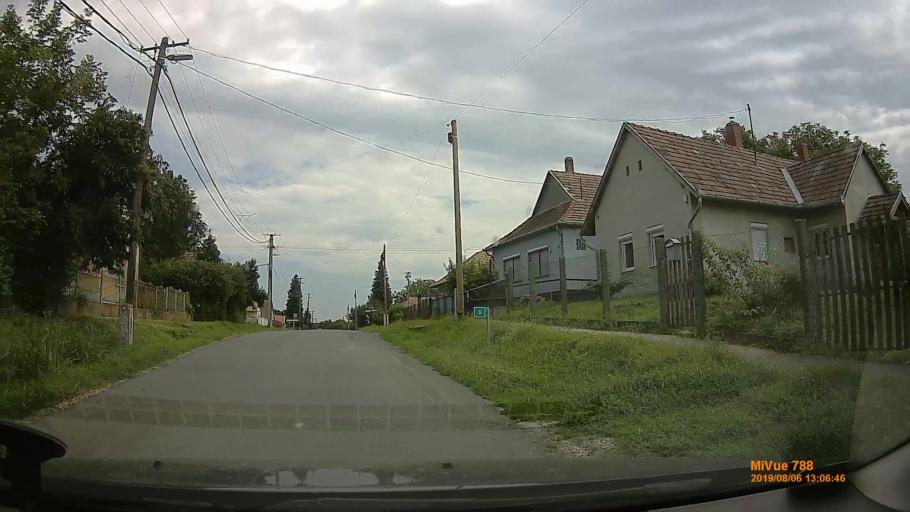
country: HU
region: Zala
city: Pacsa
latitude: 46.6299
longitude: 17.0558
